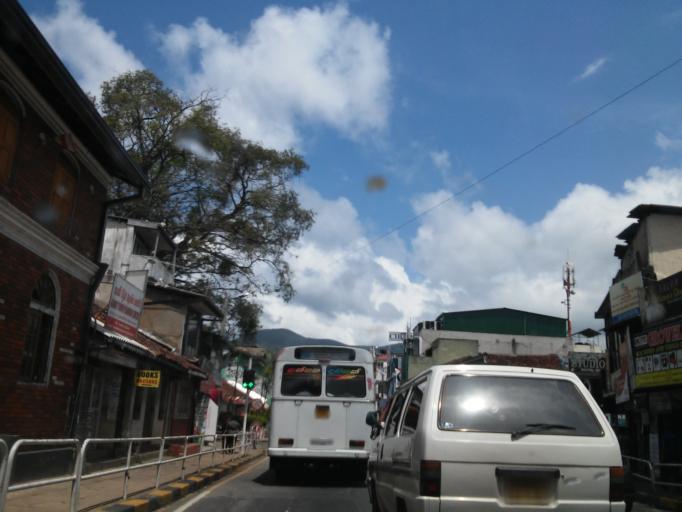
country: LK
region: Central
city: Kandy
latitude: 7.2989
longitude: 80.6369
